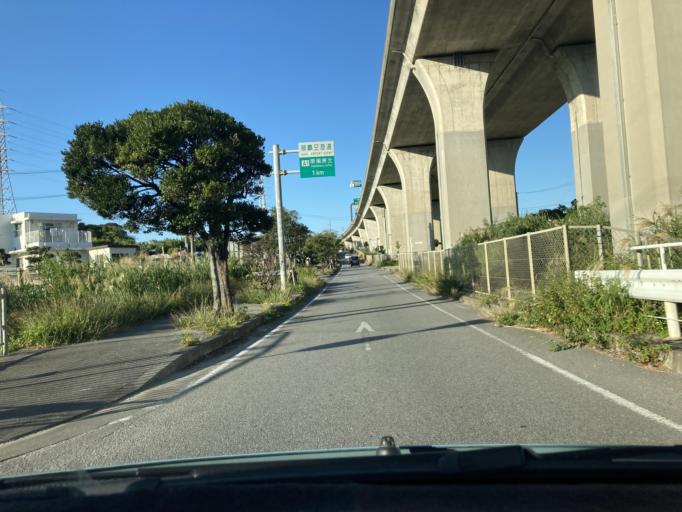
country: JP
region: Okinawa
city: Tomigusuku
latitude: 26.1918
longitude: 127.7389
